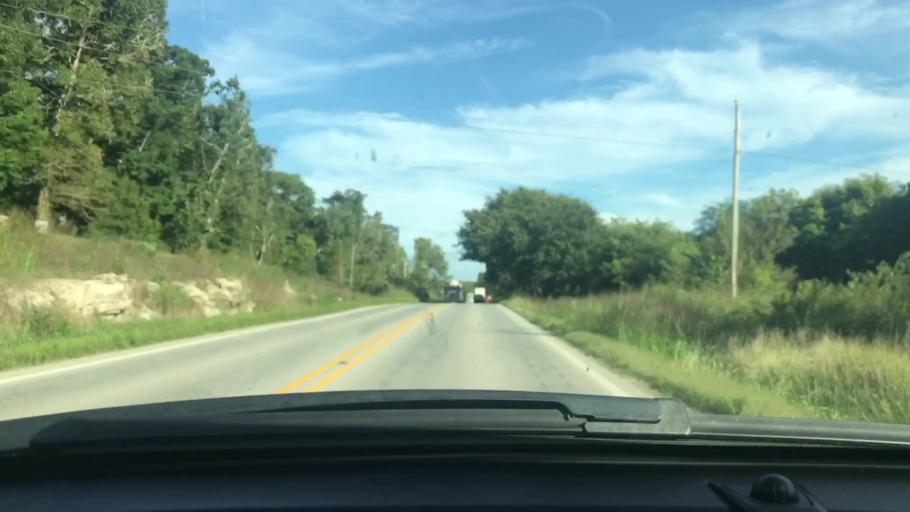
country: US
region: Arkansas
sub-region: Sharp County
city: Cherokee Village
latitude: 36.3069
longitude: -91.4542
